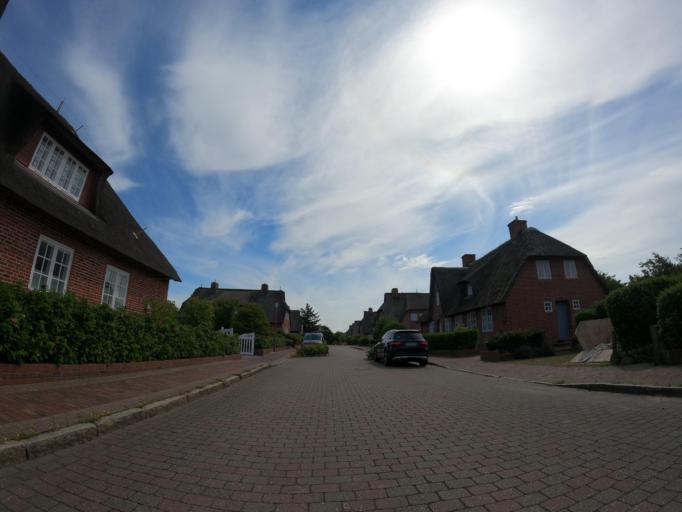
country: DE
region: Schleswig-Holstein
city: Westerland
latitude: 54.9200
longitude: 8.3101
